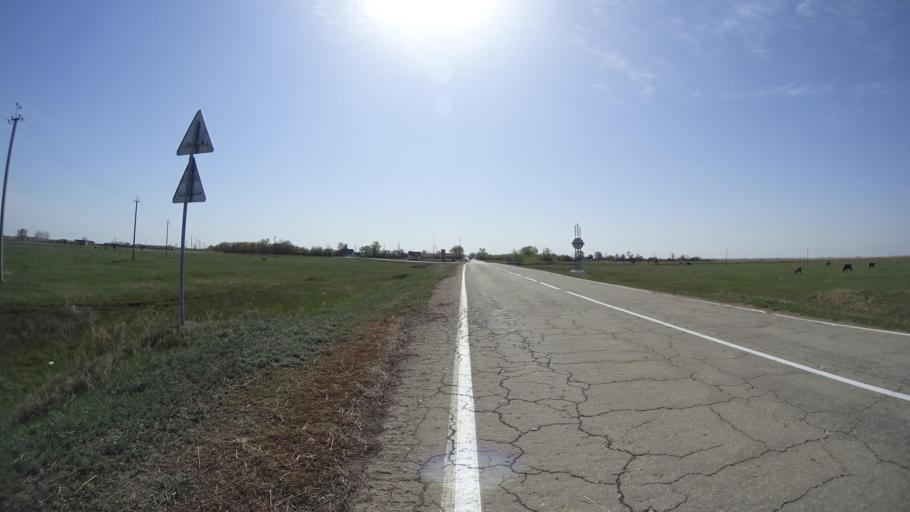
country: RU
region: Chelyabinsk
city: Chesma
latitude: 53.8034
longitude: 61.0128
